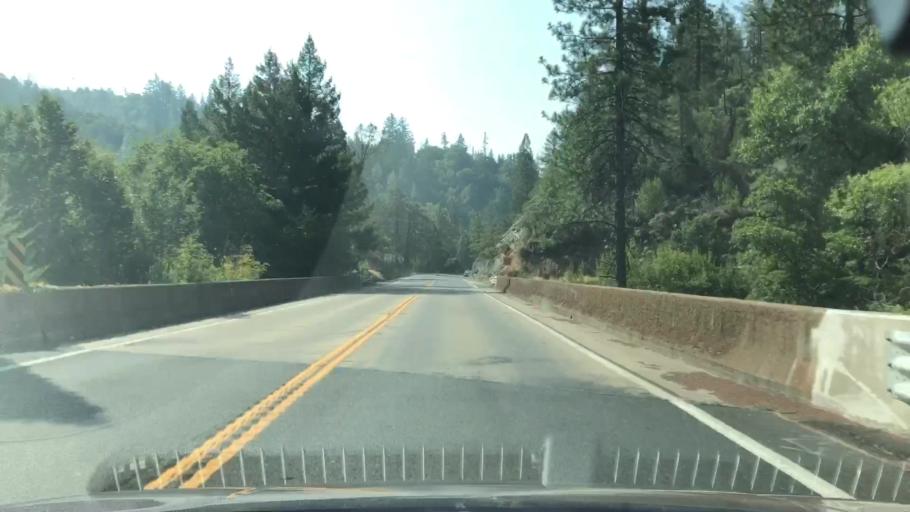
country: US
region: California
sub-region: Lake County
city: Middletown
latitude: 38.6814
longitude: -122.5915
